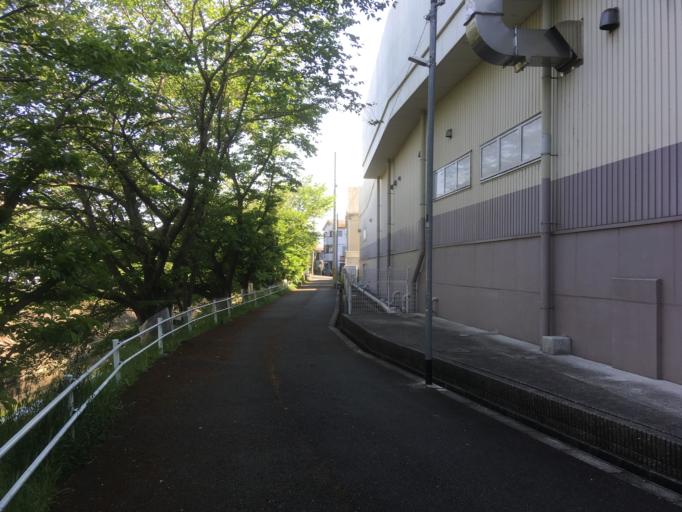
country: JP
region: Nara
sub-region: Ikoma-shi
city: Ikoma
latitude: 34.6839
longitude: 135.7067
